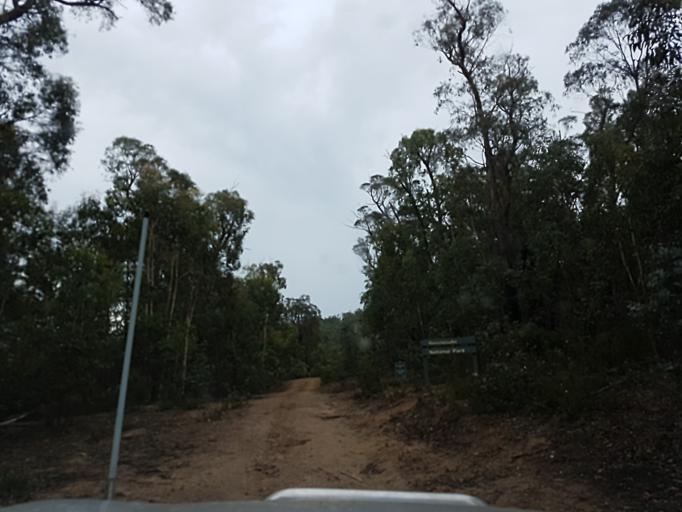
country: AU
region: New South Wales
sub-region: Snowy River
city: Jindabyne
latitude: -36.8509
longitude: 148.3356
